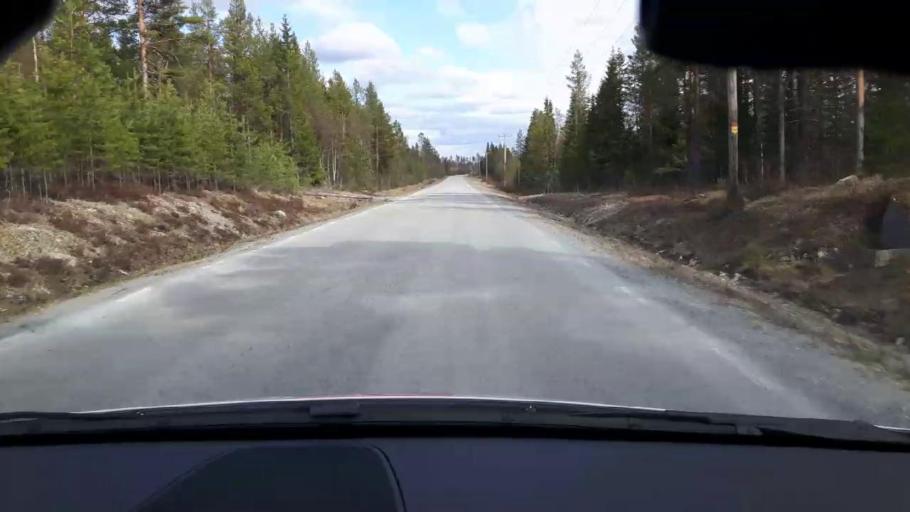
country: SE
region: Jaemtland
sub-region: Bergs Kommun
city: Hoverberg
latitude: 62.6823
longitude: 14.6483
